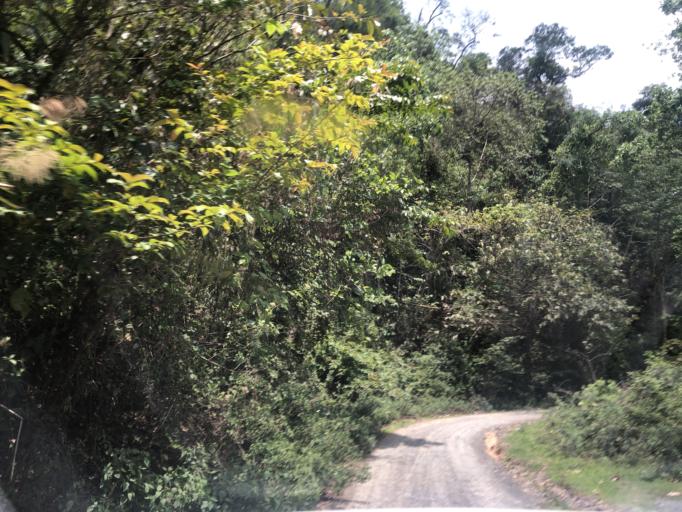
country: LA
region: Phongsali
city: Phongsali
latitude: 21.4479
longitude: 102.1631
